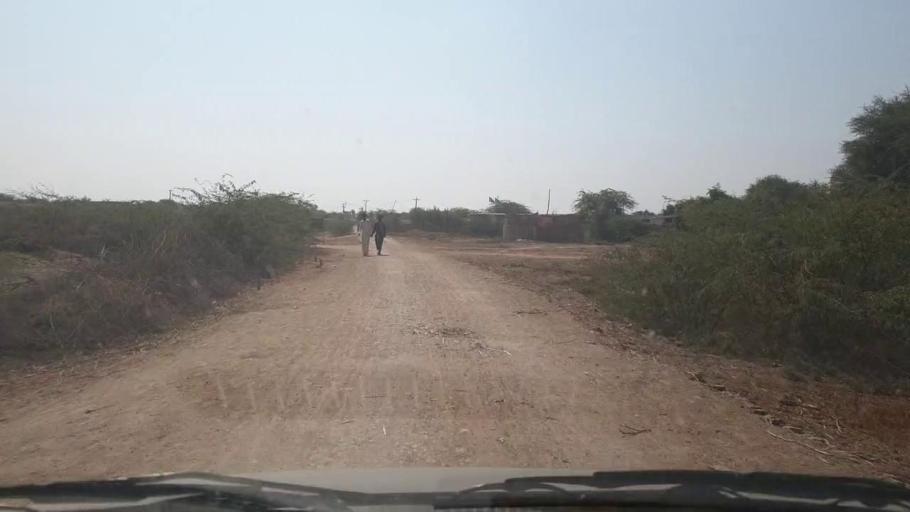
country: PK
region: Sindh
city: Samaro
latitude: 25.2591
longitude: 69.3342
